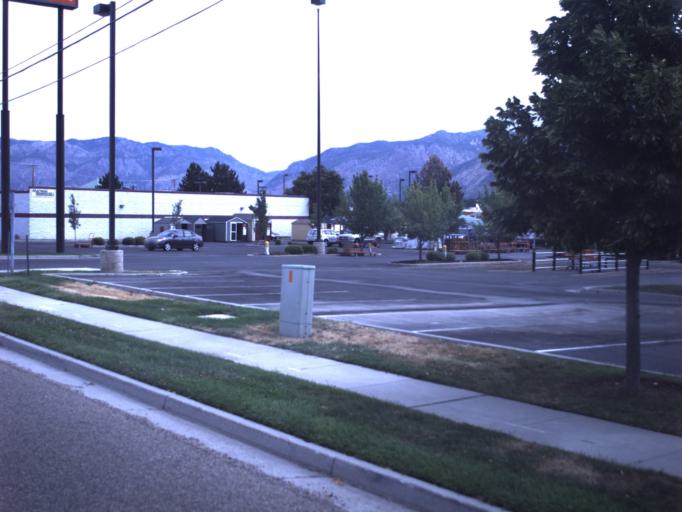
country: US
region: Utah
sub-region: Weber County
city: Riverdale
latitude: 41.1755
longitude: -112.0041
